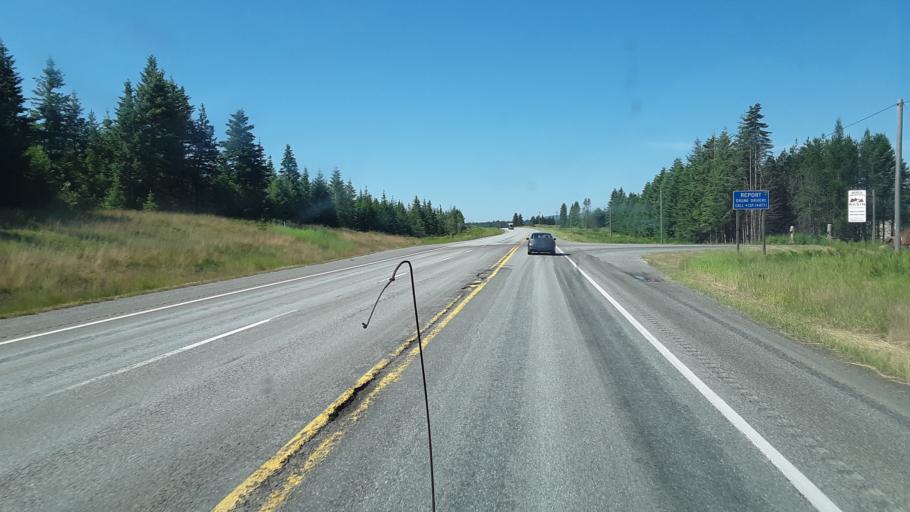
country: US
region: Idaho
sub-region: Kootenai County
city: Spirit Lake
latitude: 48.0064
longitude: -116.6690
